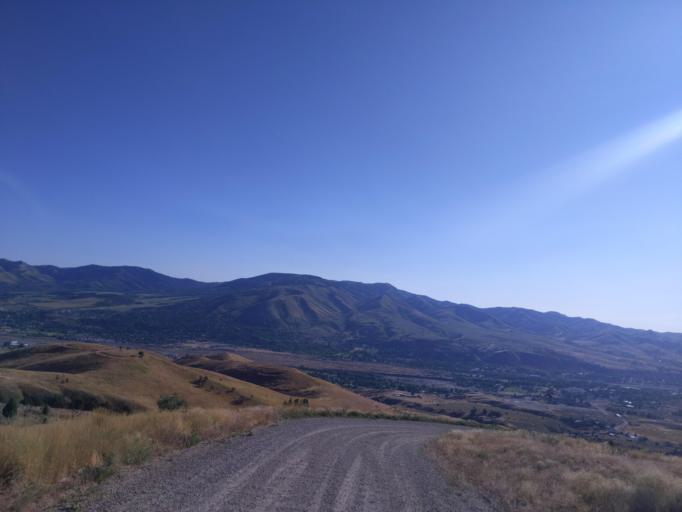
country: US
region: Idaho
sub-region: Bannock County
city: Pocatello
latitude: 42.8535
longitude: -112.3842
